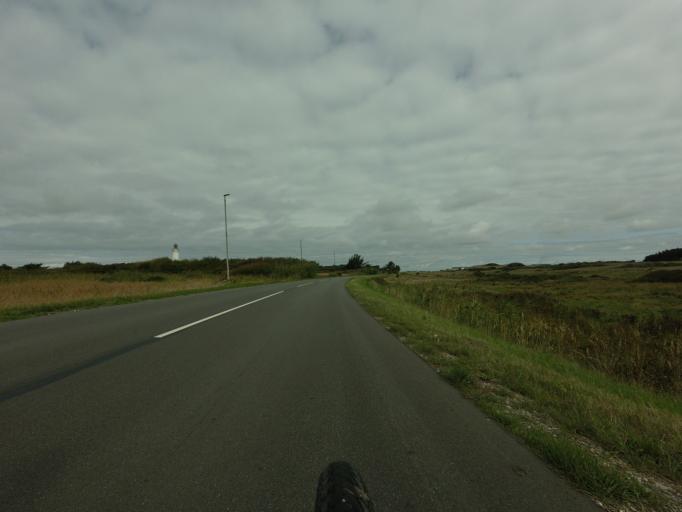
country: DK
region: North Denmark
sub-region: Hjorring Kommune
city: Hirtshals
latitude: 57.5819
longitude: 9.9440
